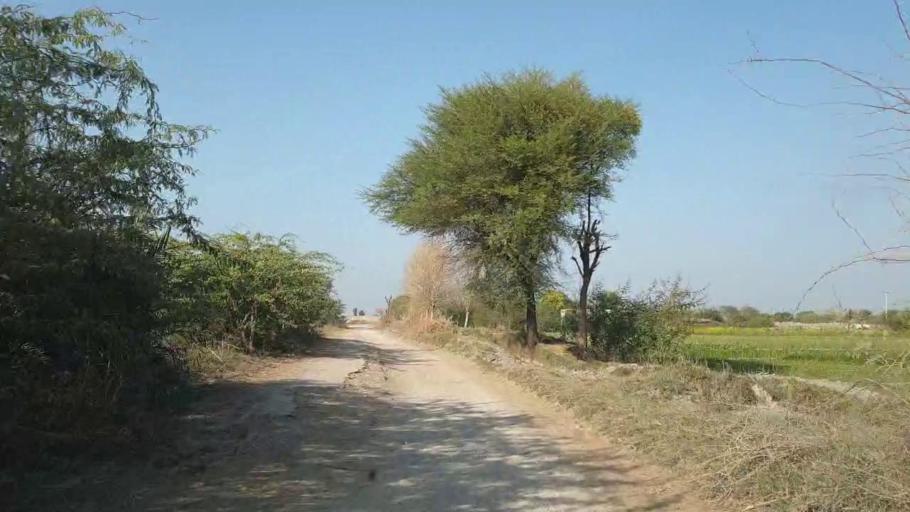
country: PK
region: Sindh
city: Tando Mittha Khan
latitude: 25.7707
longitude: 69.1937
